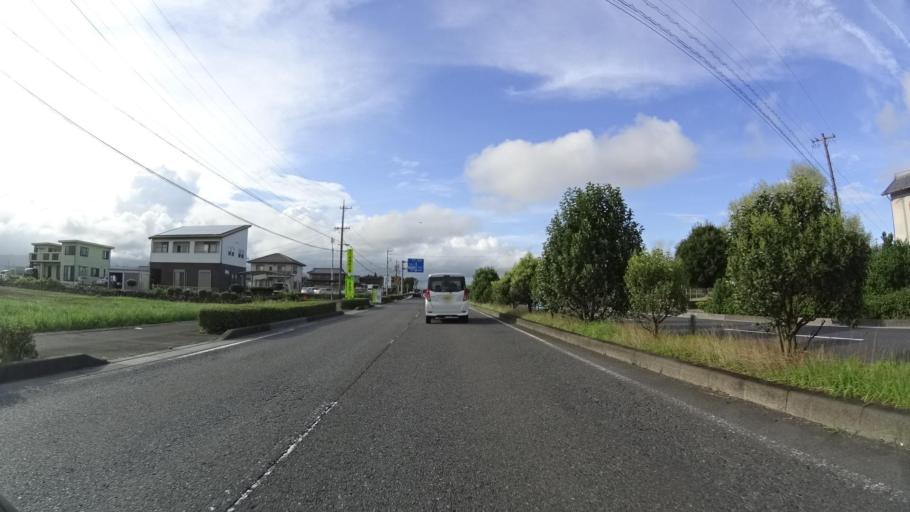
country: JP
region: Mie
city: Kameyama
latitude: 34.8992
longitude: 136.5035
